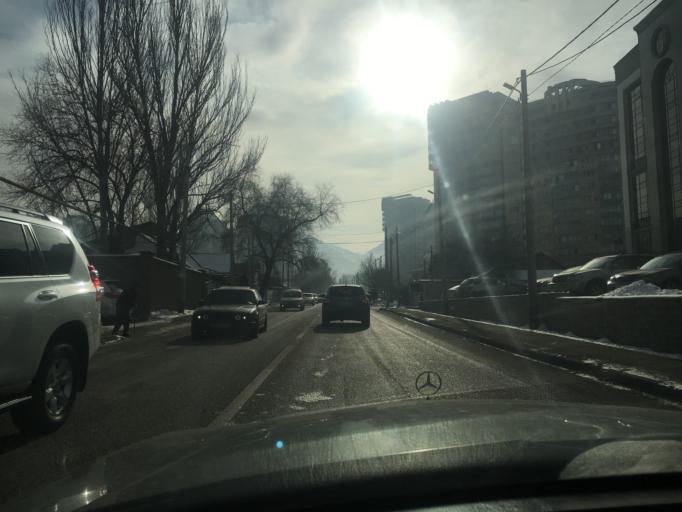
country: KZ
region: Almaty Qalasy
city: Almaty
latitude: 43.2198
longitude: 76.8805
